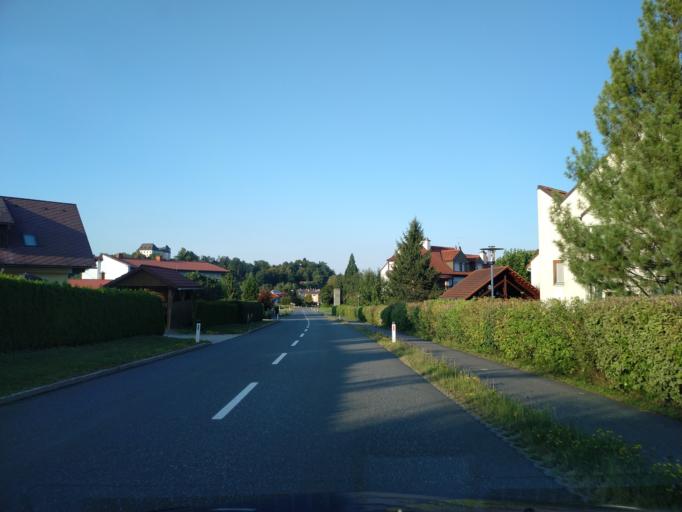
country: AT
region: Styria
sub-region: Politischer Bezirk Deutschlandsberg
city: Wies
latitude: 46.7136
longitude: 15.2600
